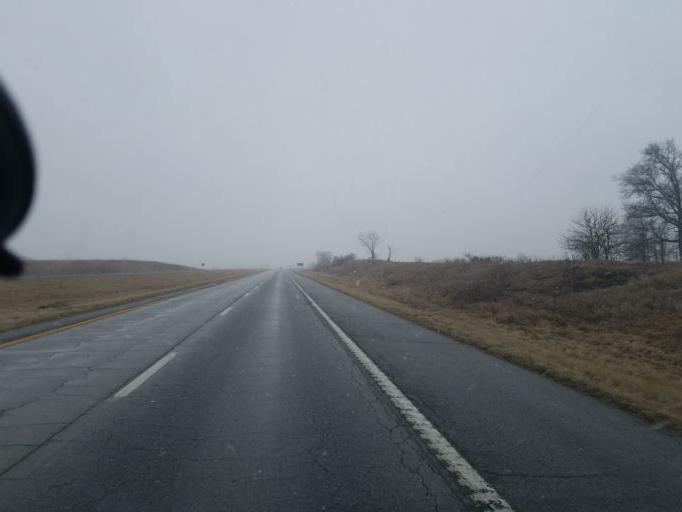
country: US
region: Missouri
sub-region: Macon County
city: La Plata
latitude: 39.9887
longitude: -92.4759
